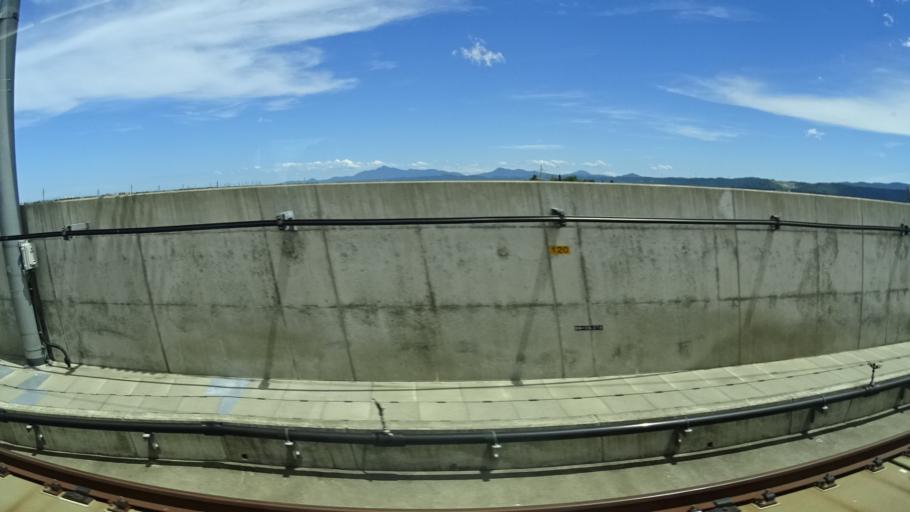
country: JP
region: Niigata
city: Joetsu
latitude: 37.0752
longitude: 138.2550
